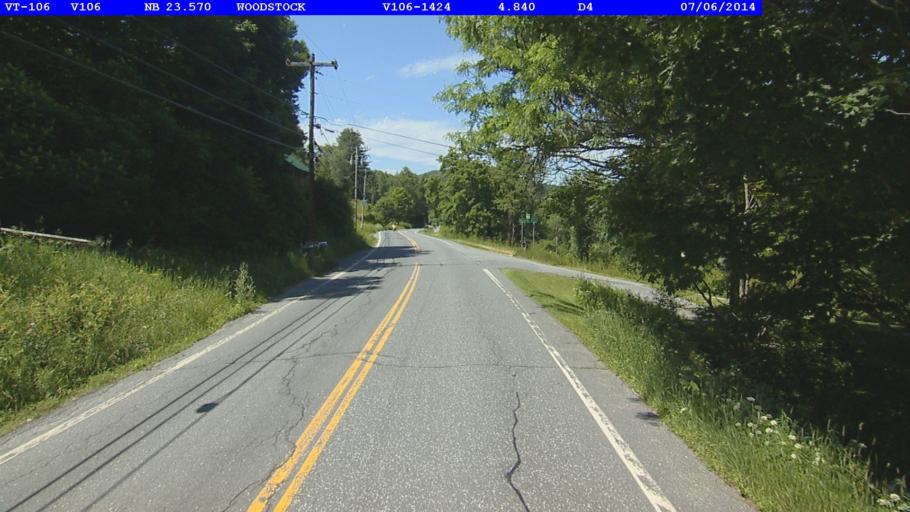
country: US
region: Vermont
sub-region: Windsor County
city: Woodstock
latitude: 43.5905
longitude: -72.5161
